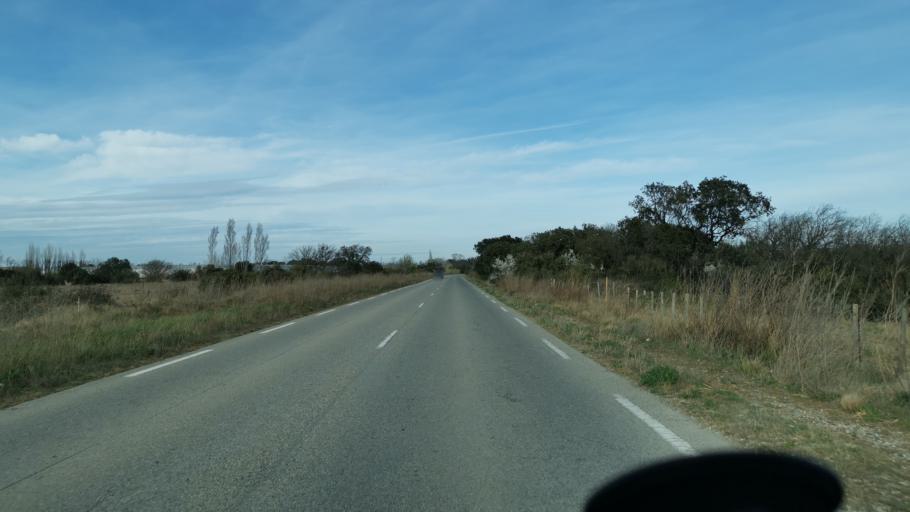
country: FR
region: Provence-Alpes-Cote d'Azur
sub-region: Departement des Bouches-du-Rhone
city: Saint-Martin-de-Crau
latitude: 43.5728
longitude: 4.7479
